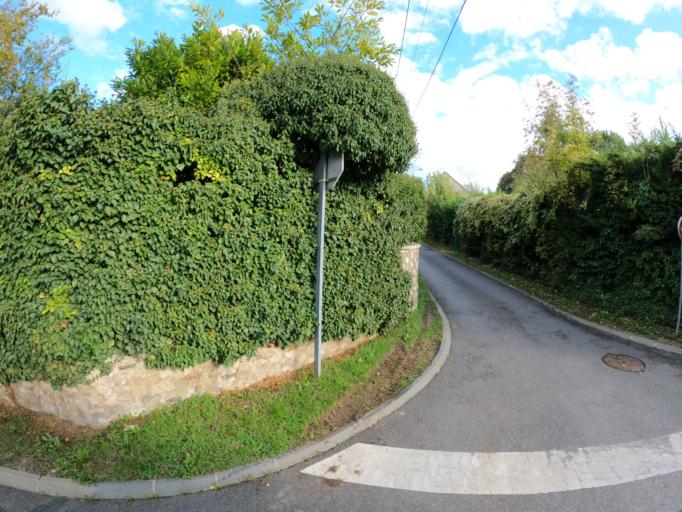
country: FR
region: Ile-de-France
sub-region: Departement de Seine-et-Marne
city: Chalifert
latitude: 48.8906
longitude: 2.7720
